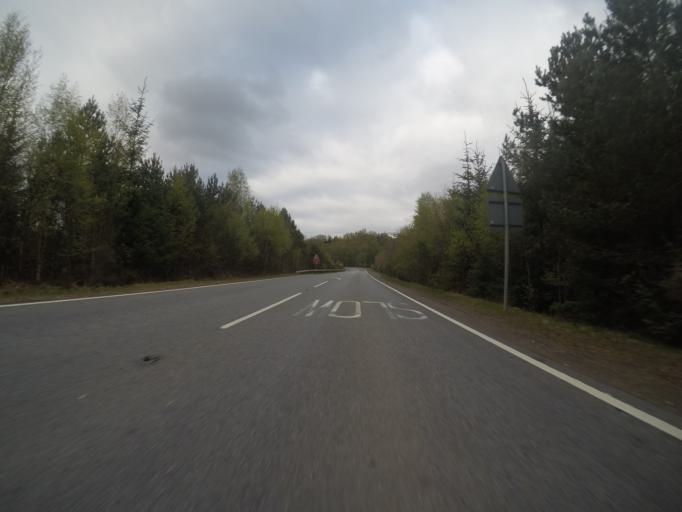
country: GB
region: Scotland
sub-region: Highland
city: Kingussie
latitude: 56.9656
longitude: -4.4466
